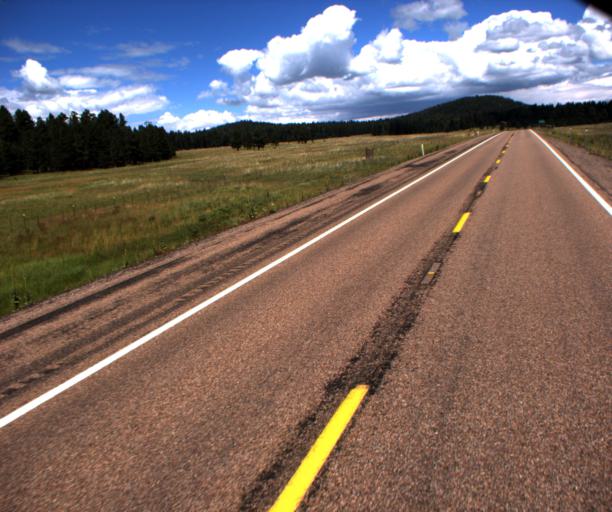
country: US
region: Arizona
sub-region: Apache County
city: Eagar
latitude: 34.0515
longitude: -109.5758
